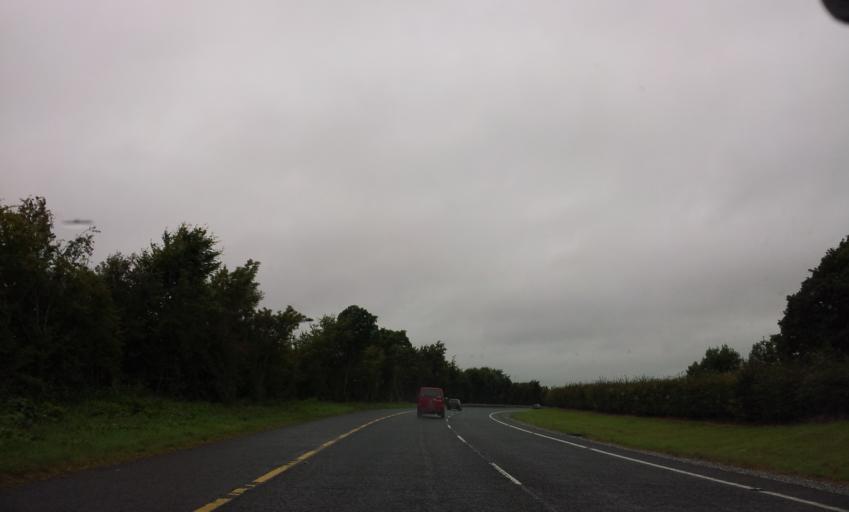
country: IE
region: Munster
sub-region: County Cork
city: Passage West
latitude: 51.9189
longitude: -8.3835
